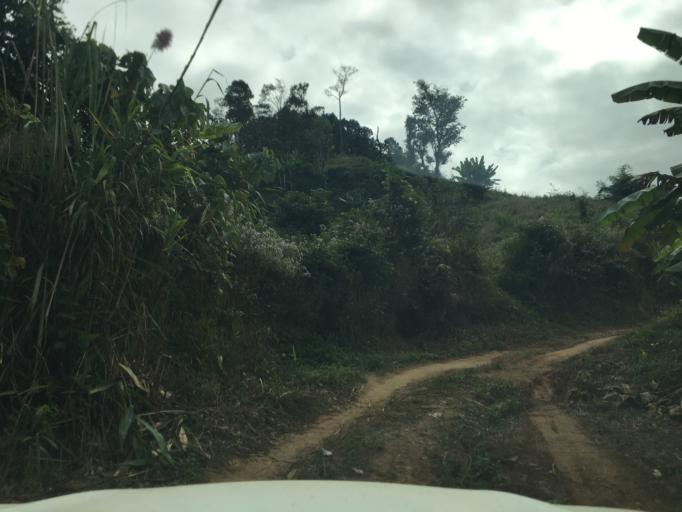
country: LA
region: Houaphan
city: Viengthong
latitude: 19.9192
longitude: 103.2984
